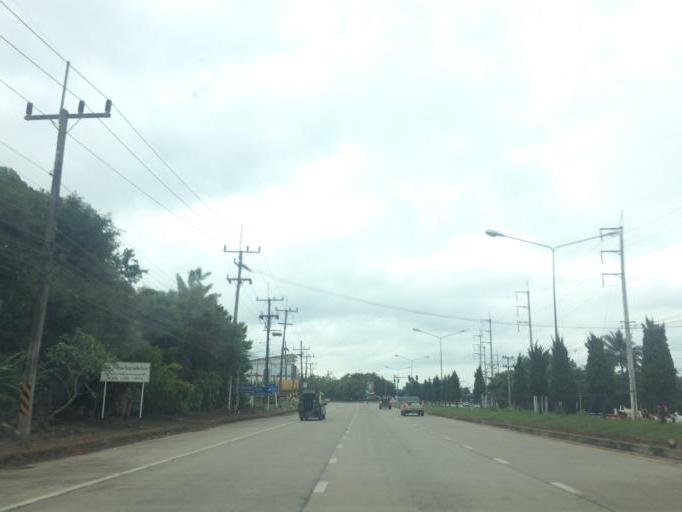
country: TH
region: Chiang Rai
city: Mae Chan
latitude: 20.1365
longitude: 99.8584
